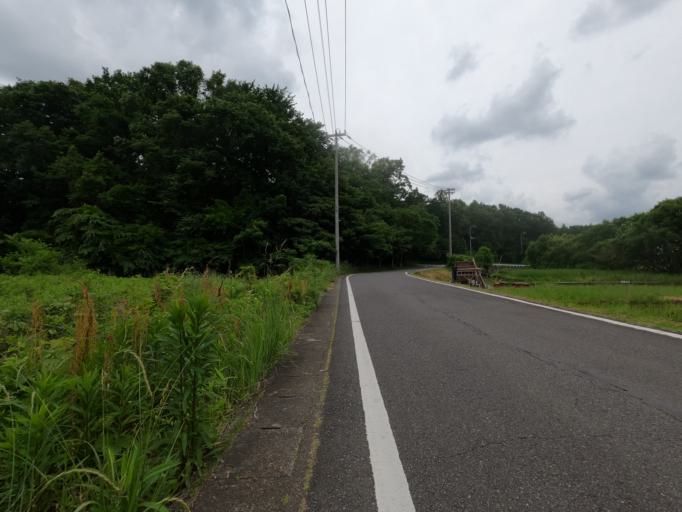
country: JP
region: Ibaraki
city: Moriya
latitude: 35.9568
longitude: 139.9663
